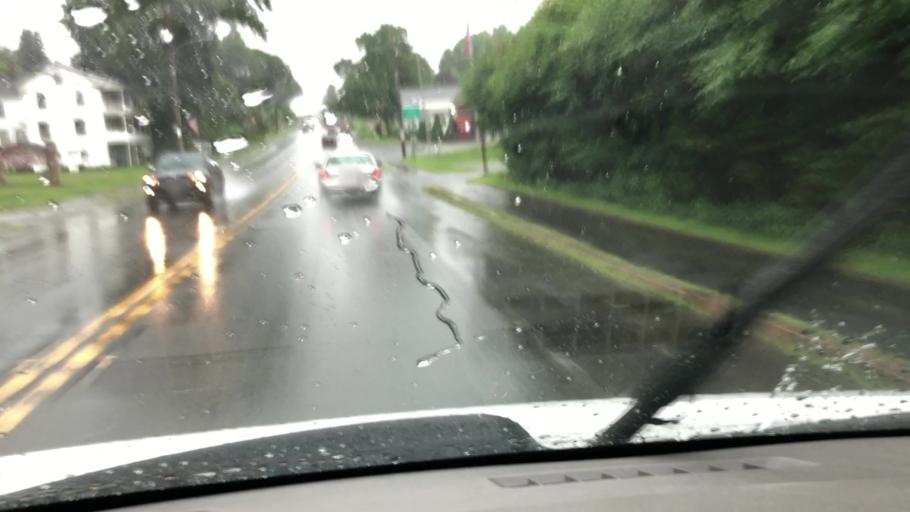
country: US
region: Massachusetts
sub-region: Berkshire County
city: Lanesborough
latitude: 42.5606
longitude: -73.1665
